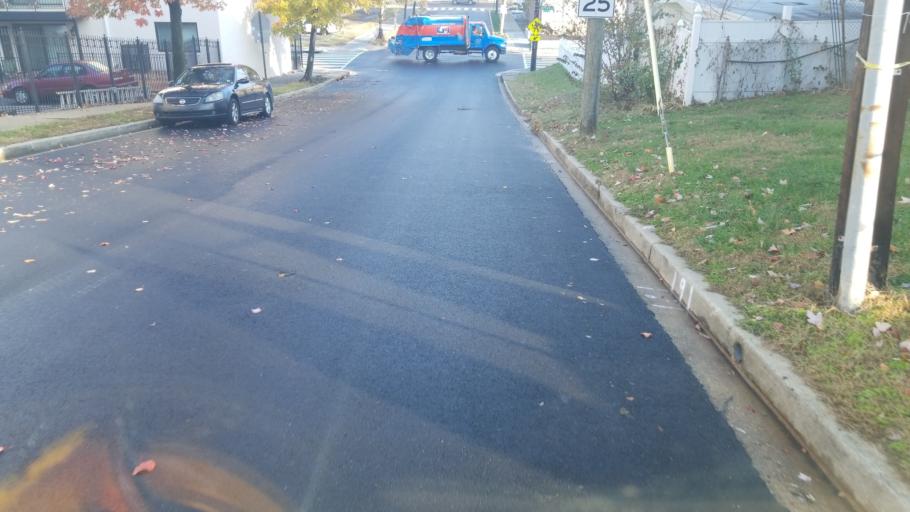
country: US
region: Maryland
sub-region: Prince George's County
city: Capitol Heights
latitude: 38.8882
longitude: -76.9300
